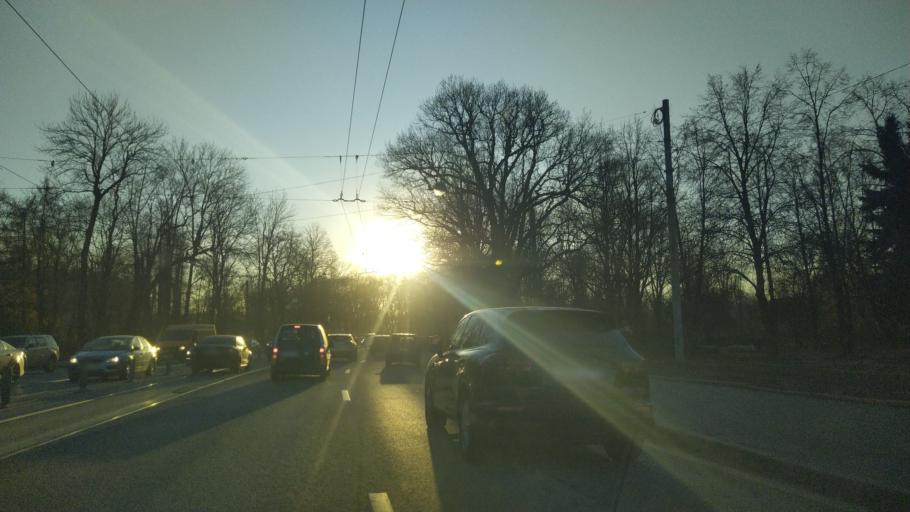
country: RU
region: Leningrad
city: Chernaya Rechka
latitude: 59.9813
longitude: 30.2999
